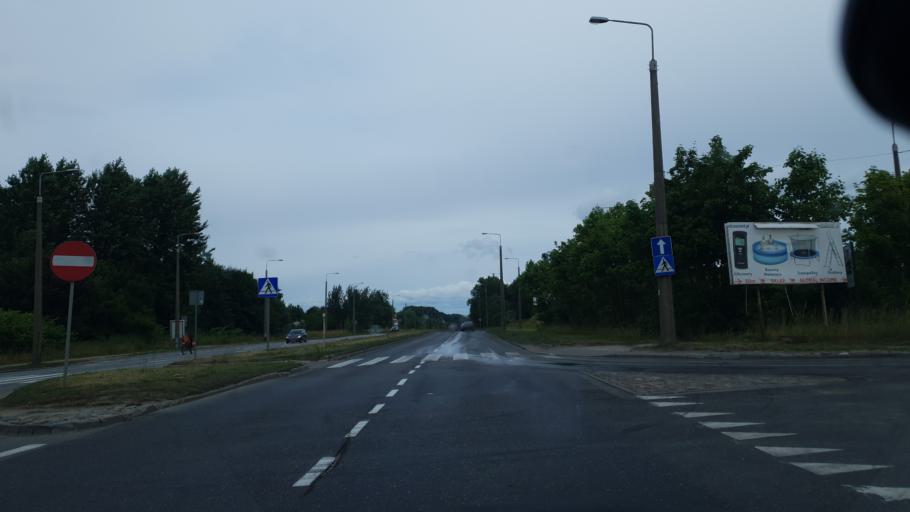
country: PL
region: Pomeranian Voivodeship
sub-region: Gdynia
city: Wielki Kack
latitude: 54.4600
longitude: 18.4558
